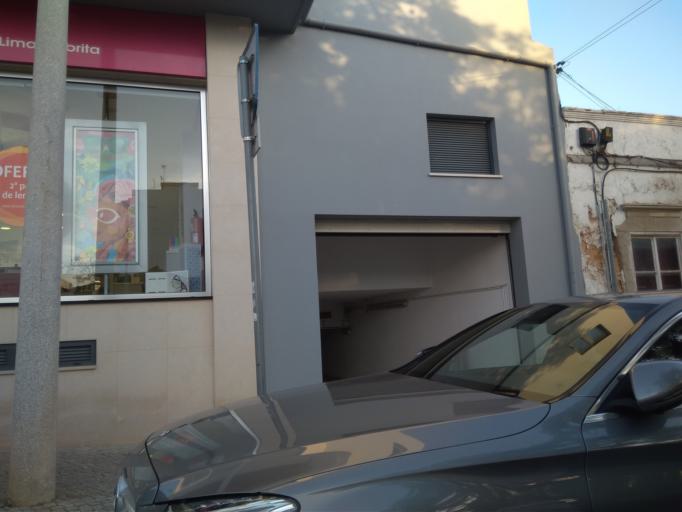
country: PT
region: Faro
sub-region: Faro
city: Faro
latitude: 37.0212
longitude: -7.9374
